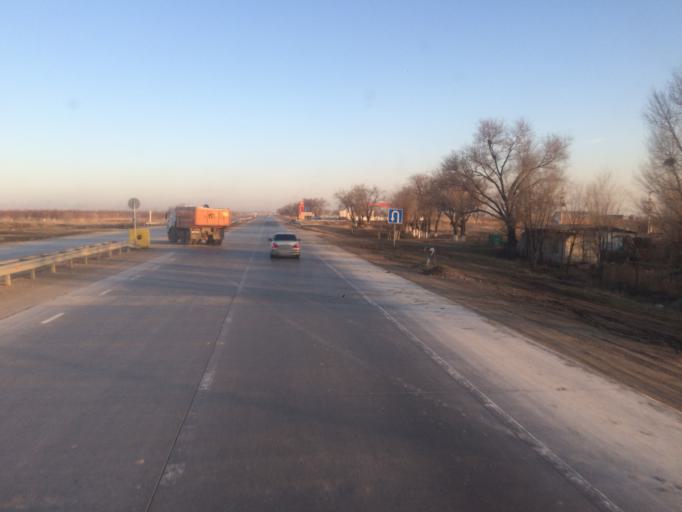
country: KZ
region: Ongtustik Qazaqstan
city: Turkestan
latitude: 43.2709
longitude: 68.3478
